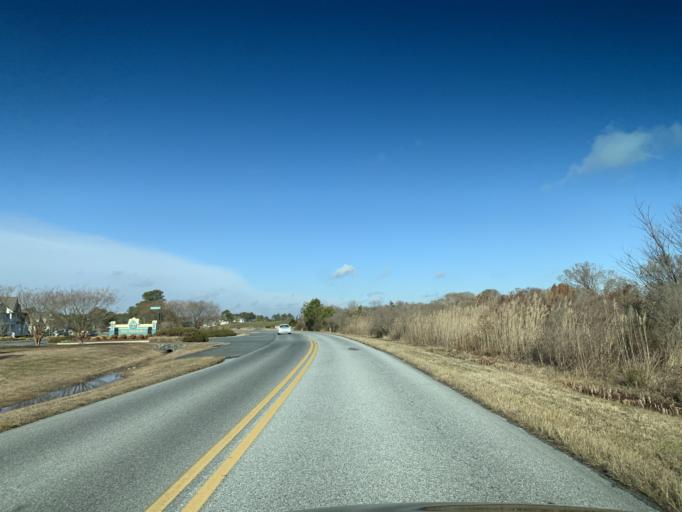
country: US
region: Maryland
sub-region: Worcester County
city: Ocean Pines
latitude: 38.4076
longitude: -75.1089
